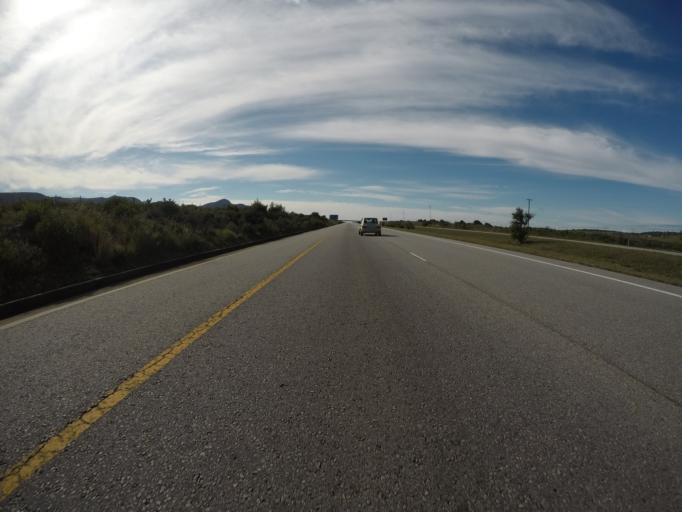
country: ZA
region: Eastern Cape
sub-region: Nelson Mandela Bay Metropolitan Municipality
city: Uitenhage
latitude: -33.9102
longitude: 25.2106
